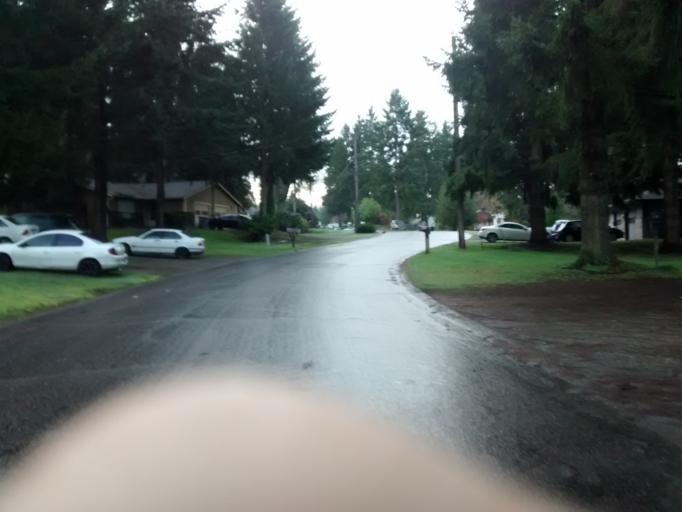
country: US
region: Washington
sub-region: Pierce County
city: Waller
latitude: 47.1961
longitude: -122.3607
